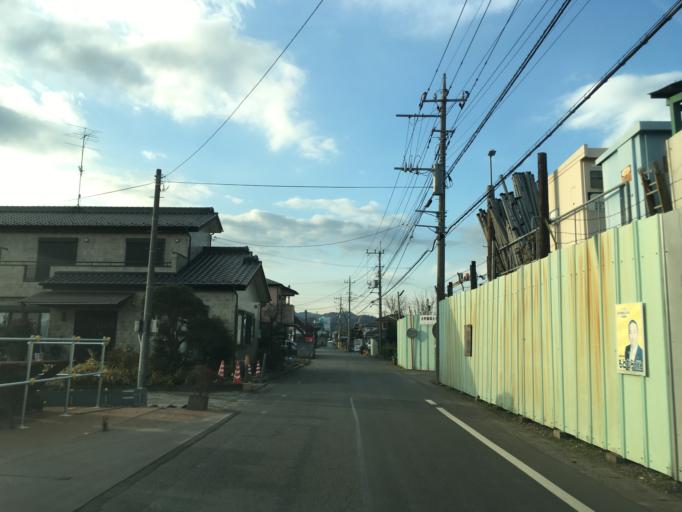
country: JP
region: Kanagawa
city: Zama
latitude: 35.5395
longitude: 139.3459
